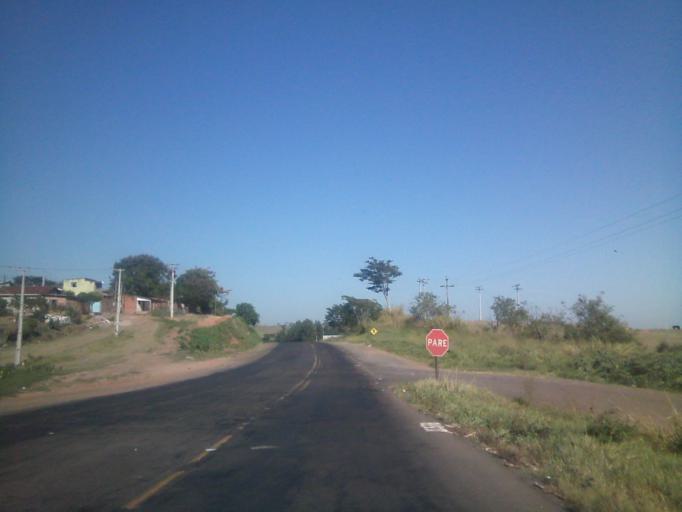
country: BR
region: Sao Paulo
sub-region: Pirapozinho
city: Pirapozinho
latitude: -22.2686
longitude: -51.5068
